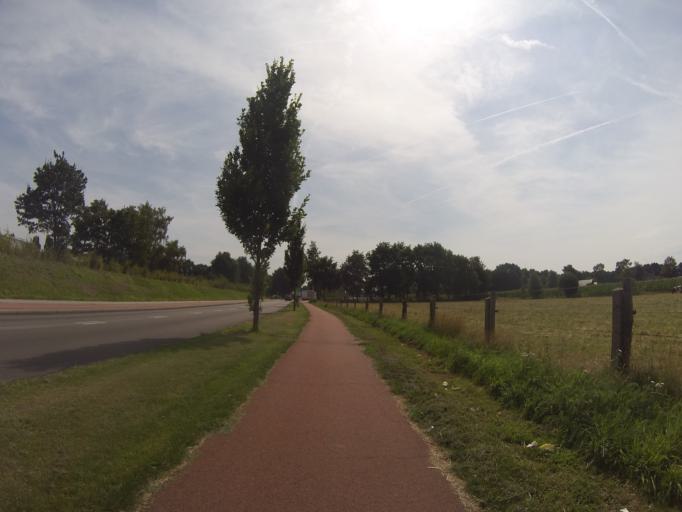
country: NL
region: Gelderland
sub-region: Gemeente Putten
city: Putten
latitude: 52.2540
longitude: 5.5909
